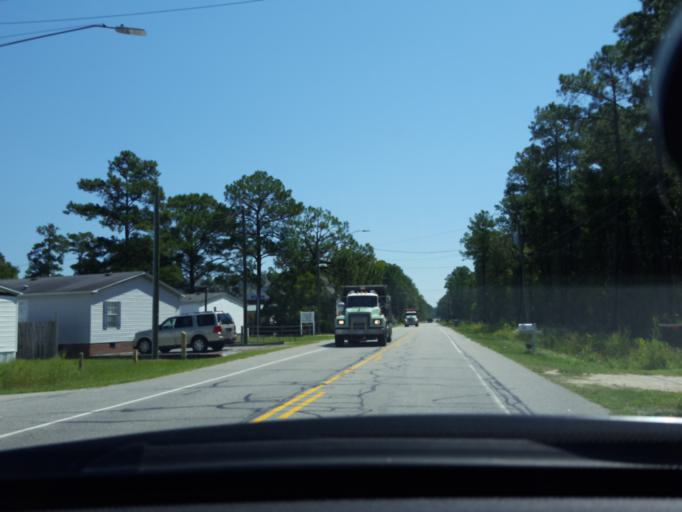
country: US
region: North Carolina
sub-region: Bladen County
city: Elizabethtown
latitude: 34.6324
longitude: -78.5051
